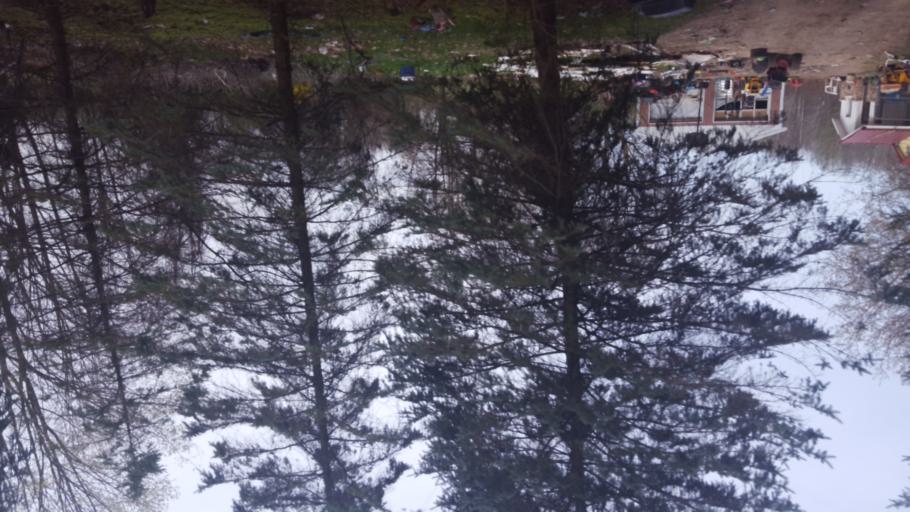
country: US
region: Michigan
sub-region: Clare County
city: Clare
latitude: 43.8783
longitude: -84.6463
